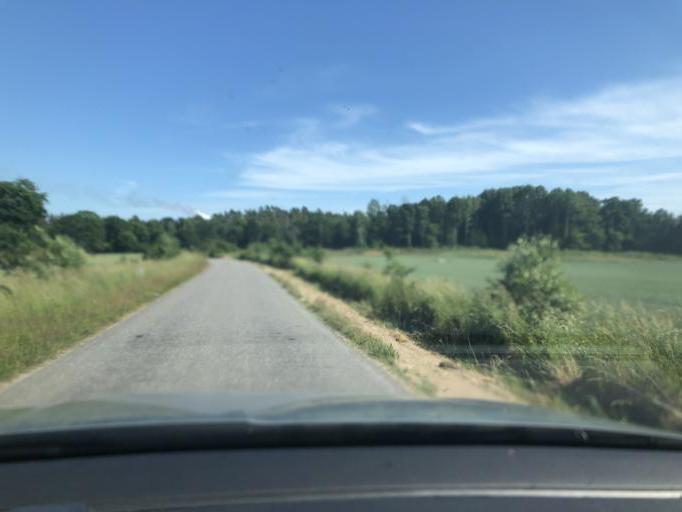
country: SE
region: Blekinge
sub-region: Karlshamns Kommun
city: Morrum
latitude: 56.1729
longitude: 14.7243
